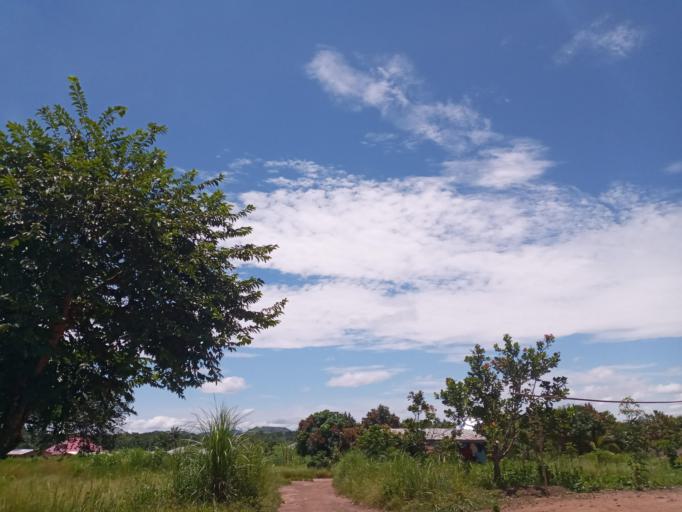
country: SL
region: Eastern Province
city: Koidu
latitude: 8.6339
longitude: -10.9405
